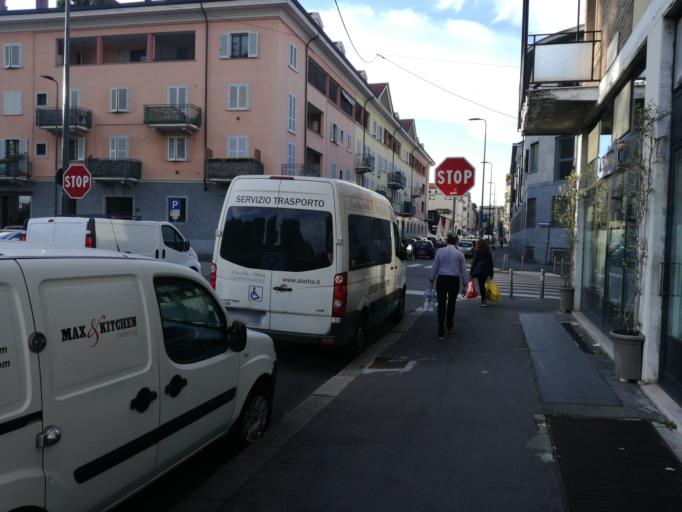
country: IT
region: Lombardy
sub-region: Citta metropolitana di Milano
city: Milano
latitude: 45.4328
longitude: 9.1807
